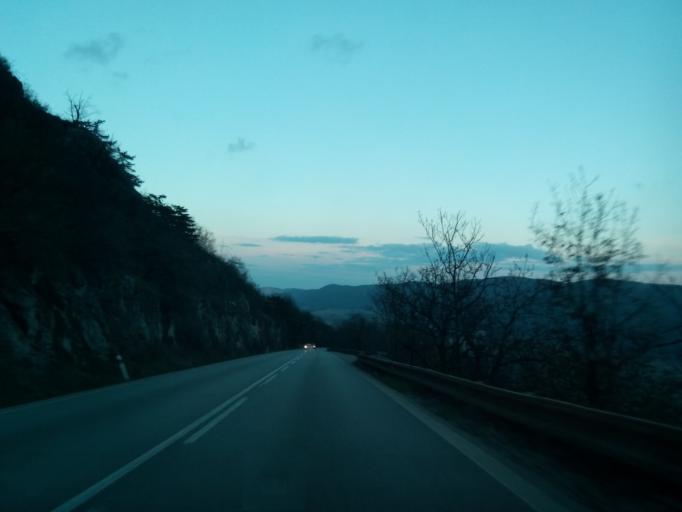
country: SK
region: Kosicky
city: Roznava
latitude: 48.6020
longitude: 20.6459
